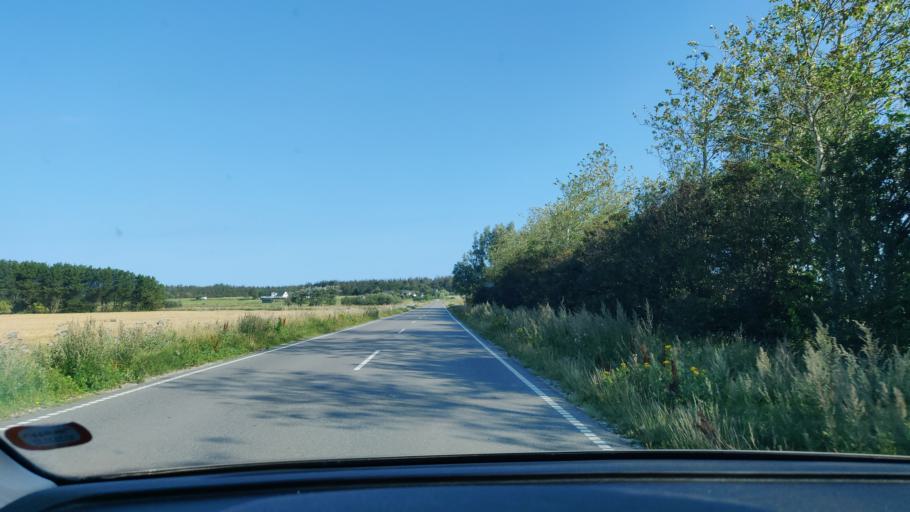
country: DK
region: North Denmark
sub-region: Jammerbugt Kommune
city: Pandrup
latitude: 57.2413
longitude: 9.6483
